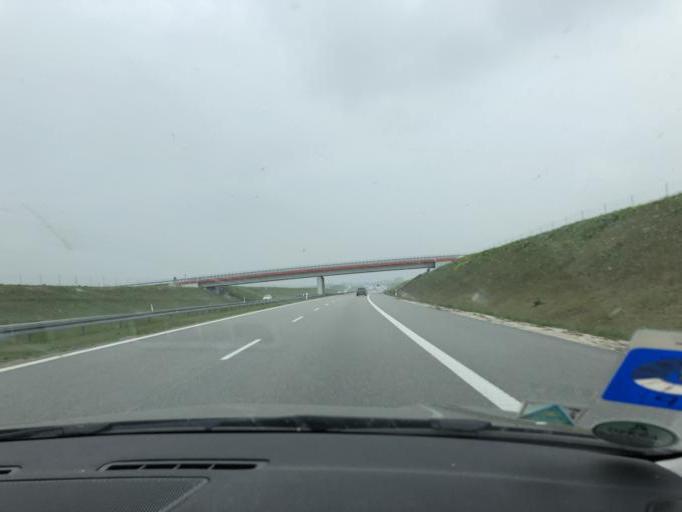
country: PL
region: Subcarpathian Voivodeship
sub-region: Powiat debicki
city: Czarna
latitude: 50.0905
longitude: 21.3015
